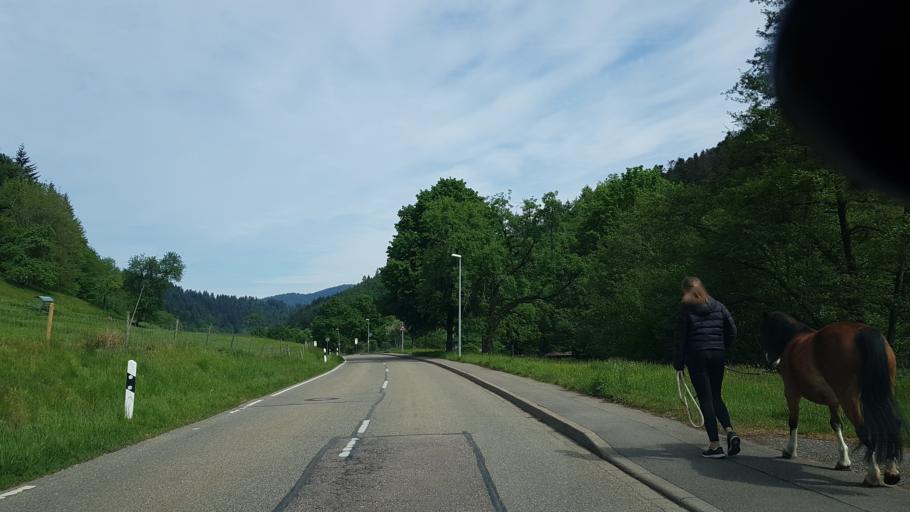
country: DE
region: Baden-Wuerttemberg
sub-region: Freiburg Region
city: Kirchzarten
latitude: 47.9546
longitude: 7.9132
